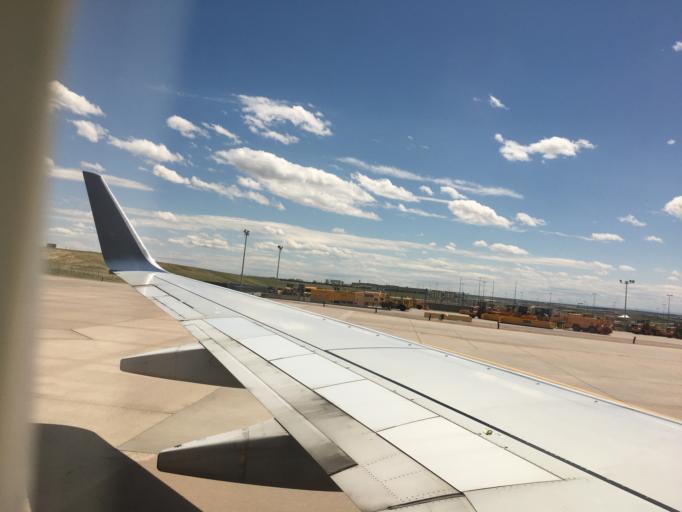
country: US
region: Colorado
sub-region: Weld County
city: Lochbuie
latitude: 39.8528
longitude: -104.6660
